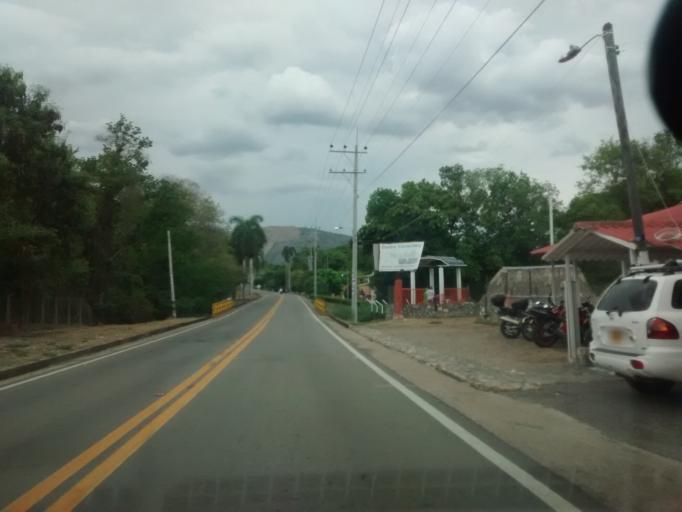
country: CO
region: Cundinamarca
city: Tocaima
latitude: 4.4512
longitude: -74.6511
